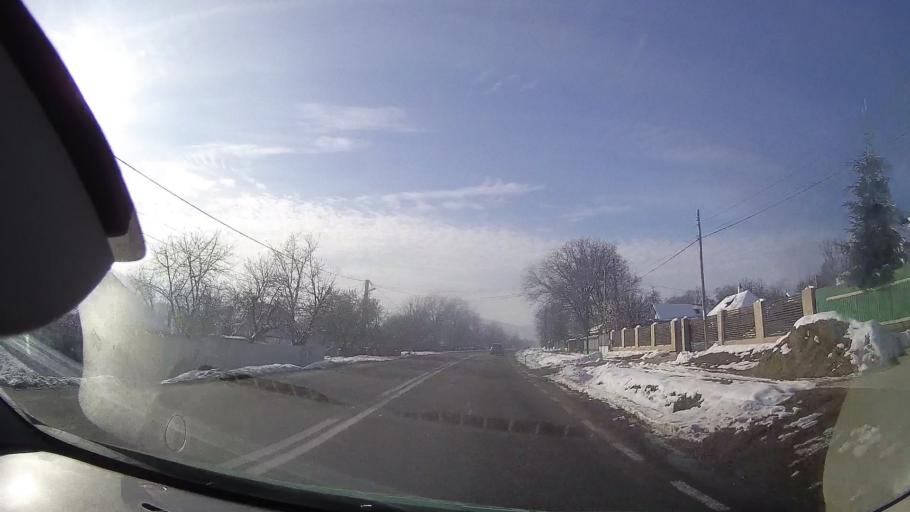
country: RO
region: Neamt
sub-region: Comuna Dobreni
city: Dobreni
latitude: 46.9973
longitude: 26.4068
